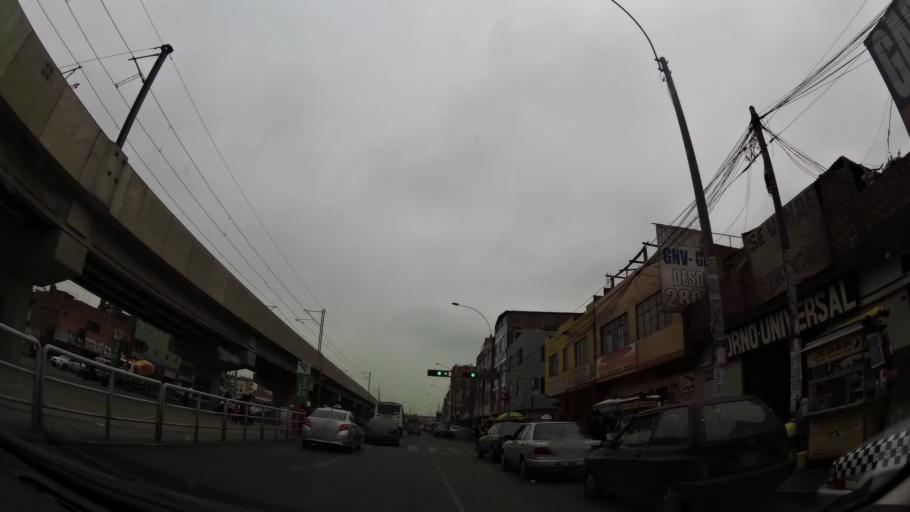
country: PE
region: Lima
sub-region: Lima
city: San Luis
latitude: -12.0754
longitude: -77.0111
